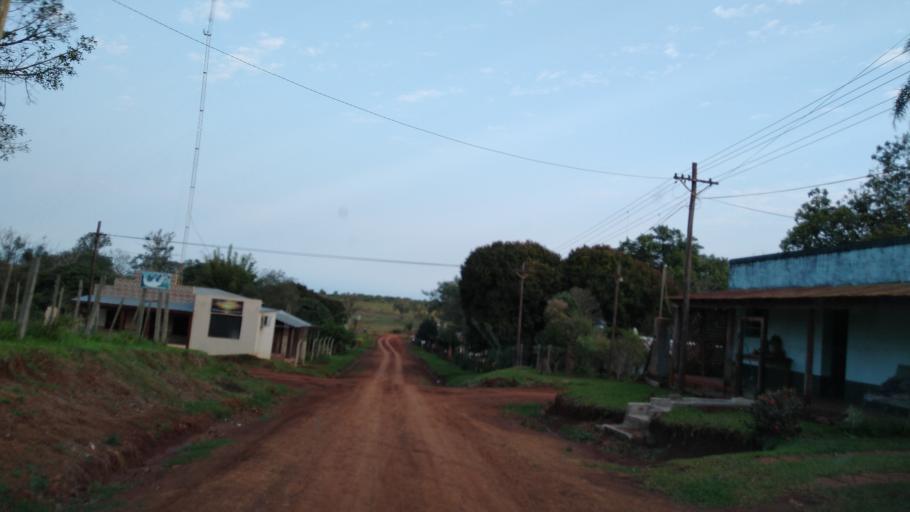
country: AR
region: Corrientes
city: San Carlos
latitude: -27.7492
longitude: -55.9009
